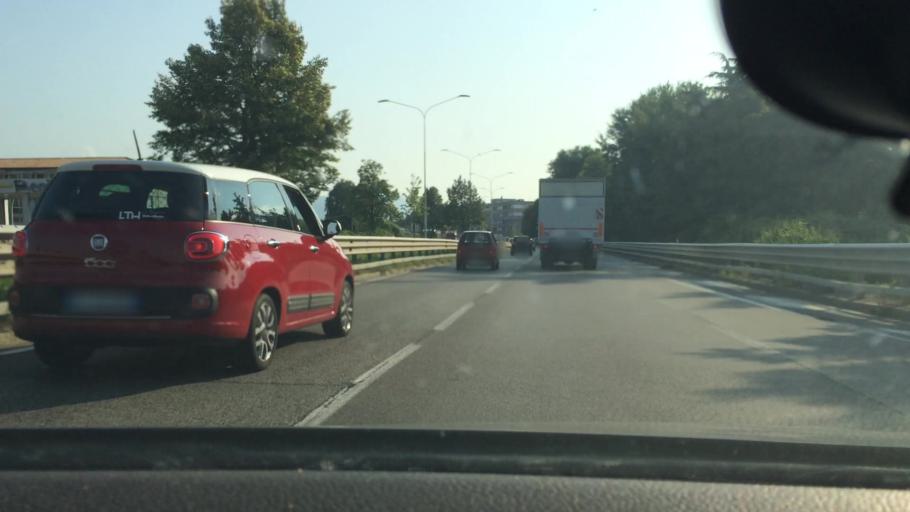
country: IT
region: Lombardy
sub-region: Provincia di Bergamo
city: Orio al Serio
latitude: 45.6858
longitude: 9.6846
